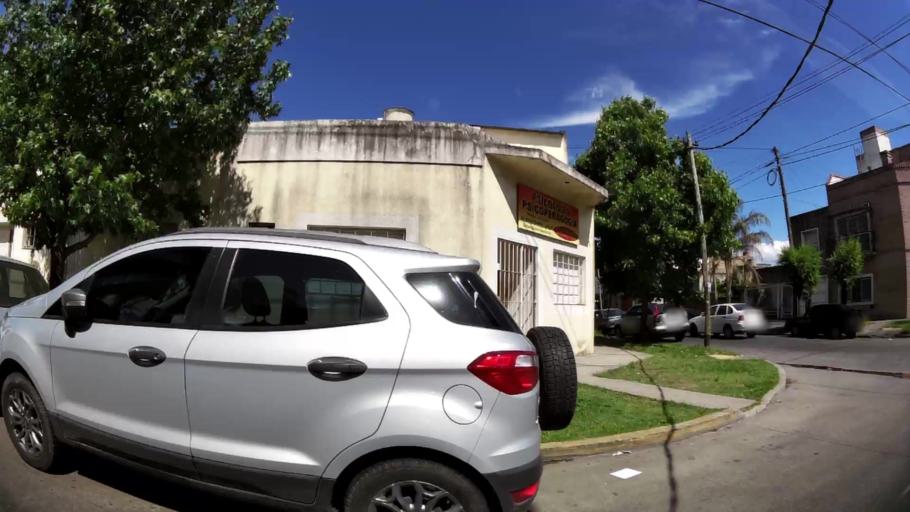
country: AR
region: Buenos Aires
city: San Justo
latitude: -34.6730
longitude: -58.5661
